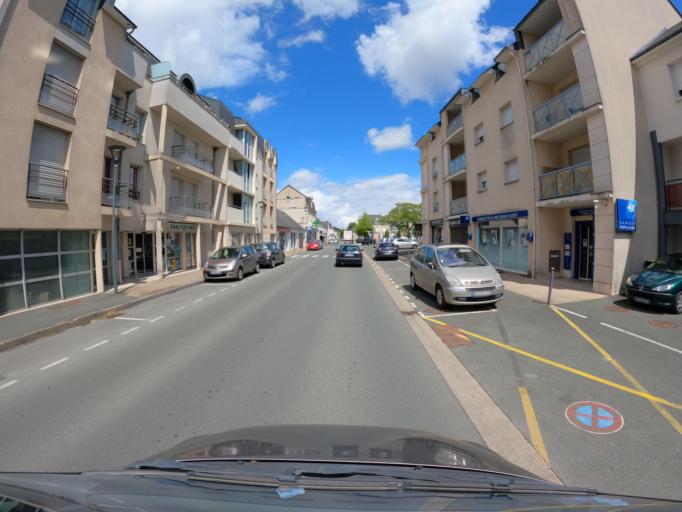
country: FR
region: Pays de la Loire
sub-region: Departement de Maine-et-Loire
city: Avrille
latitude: 47.5278
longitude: -0.6117
